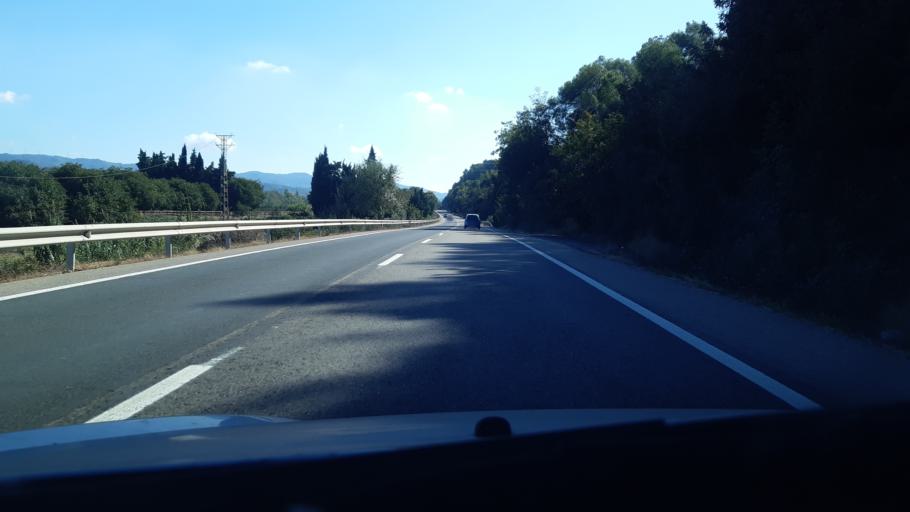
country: ES
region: Catalonia
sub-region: Provincia de Tarragona
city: Tivenys
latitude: 40.8668
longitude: 0.5046
